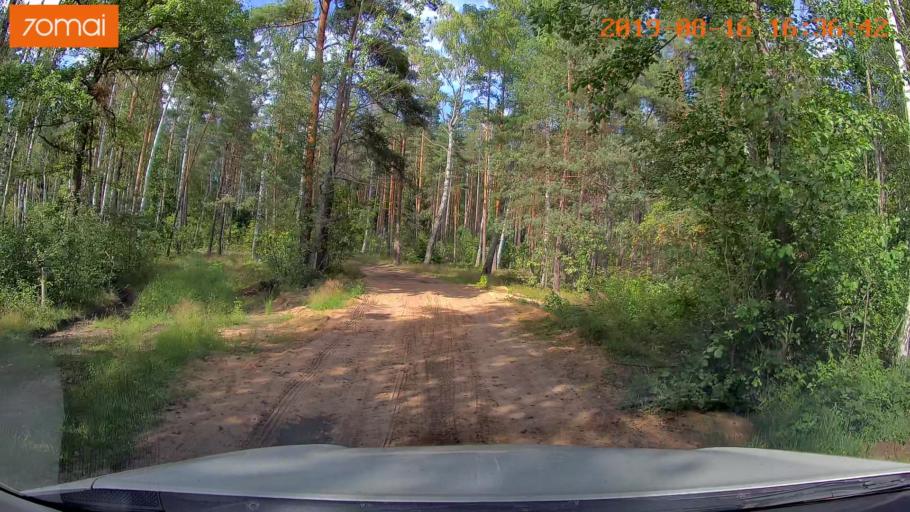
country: BY
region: Mogilev
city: Asipovichy
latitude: 53.2313
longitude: 28.7760
